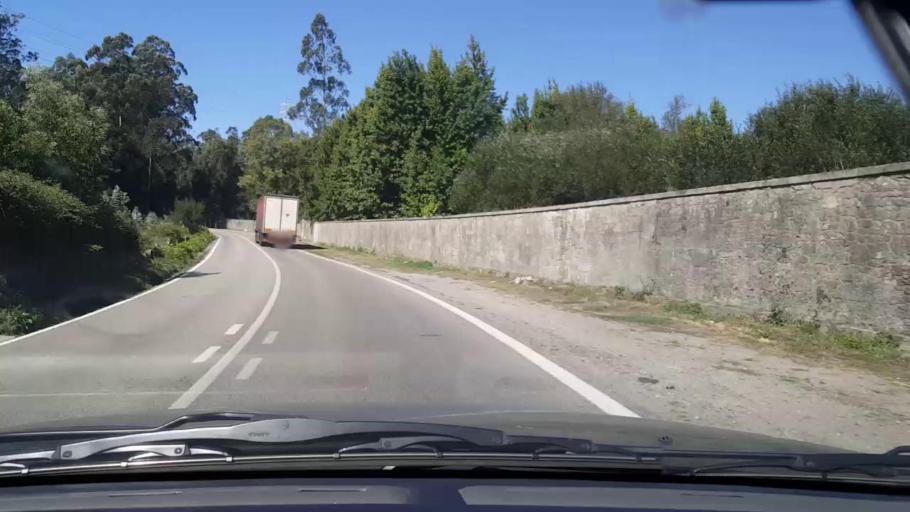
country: PT
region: Porto
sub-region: Vila do Conde
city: Arvore
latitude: 41.3395
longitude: -8.6922
